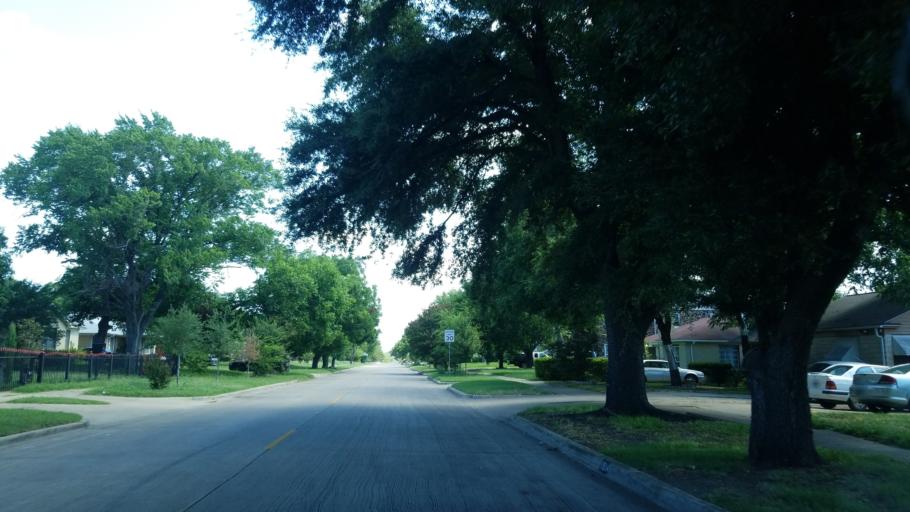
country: US
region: Texas
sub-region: Dallas County
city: Dallas
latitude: 32.7260
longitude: -96.7966
